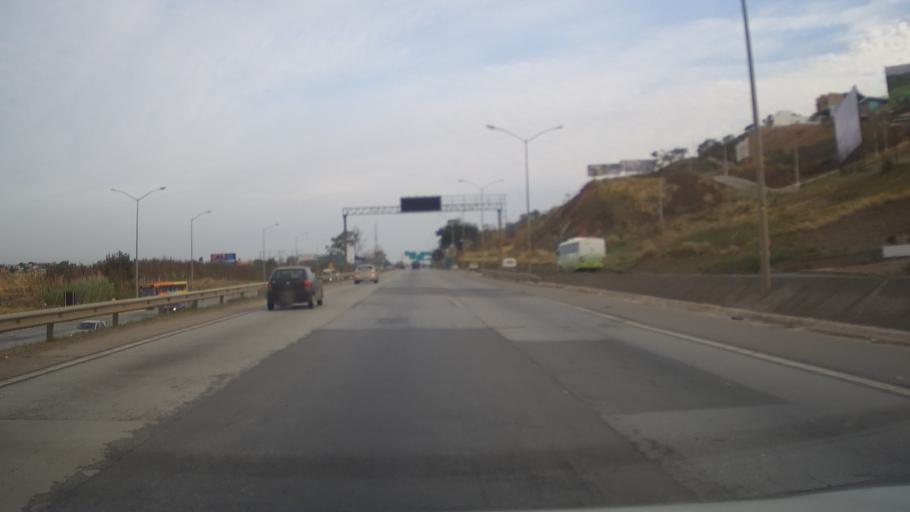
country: BR
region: Minas Gerais
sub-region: Vespasiano
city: Vespasiano
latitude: -19.7693
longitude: -43.9483
